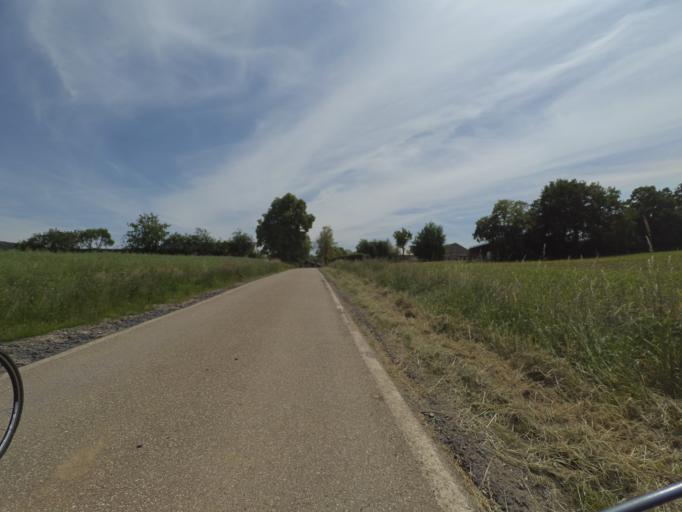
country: DE
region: Rheinland-Pfalz
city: Montenich
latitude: 50.2080
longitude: 7.3102
